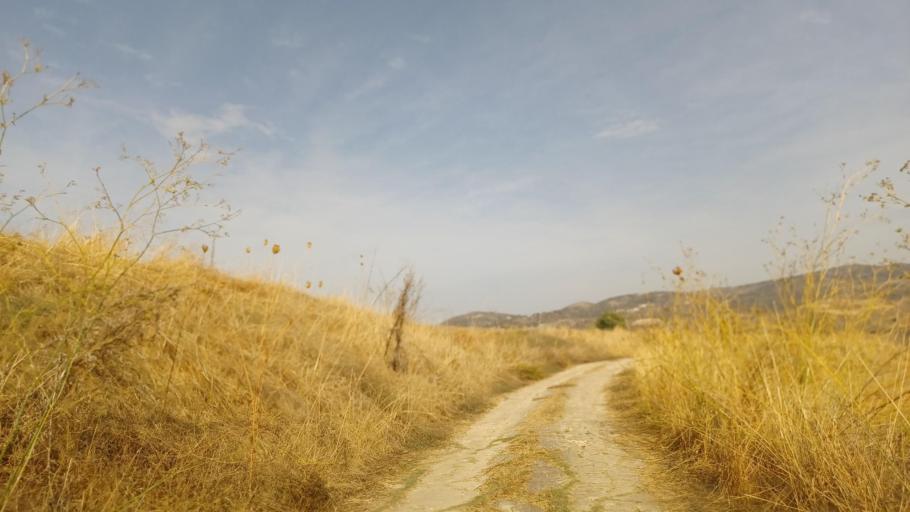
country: CY
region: Pafos
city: Polis
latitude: 34.9489
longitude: 32.5153
